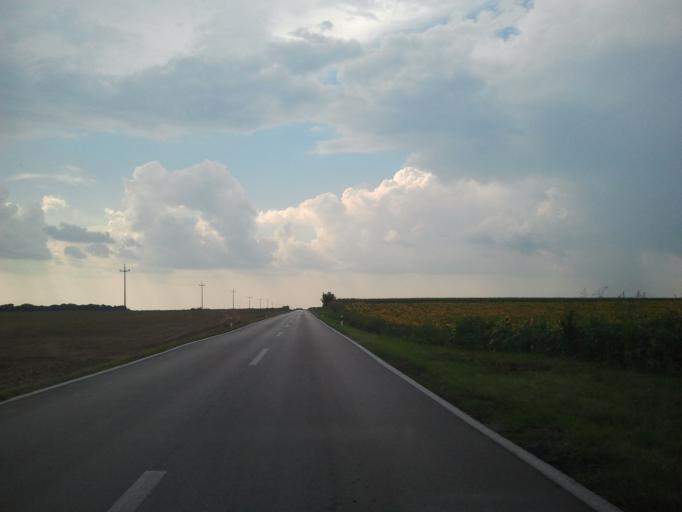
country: HR
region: Vukovarsko-Srijemska
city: Bapska
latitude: 45.2375
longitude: 19.2481
